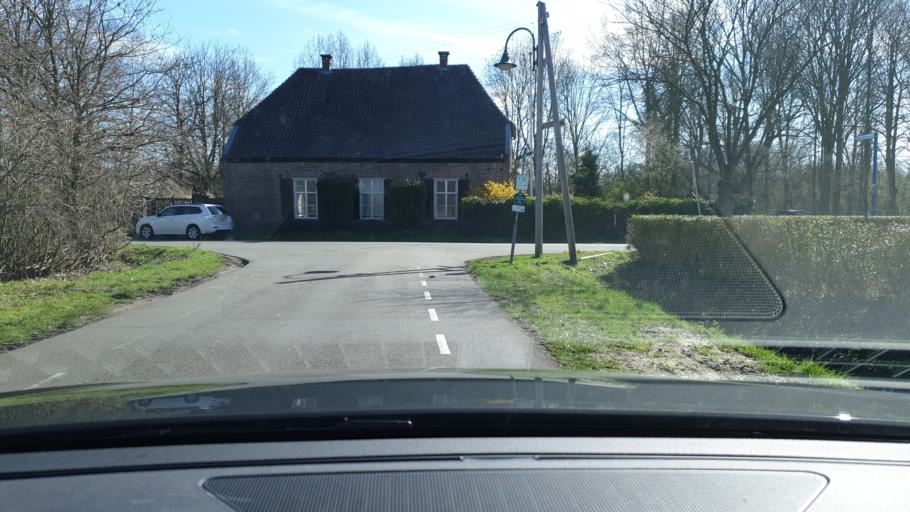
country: NL
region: North Brabant
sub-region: Gemeente Eindhoven
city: Muschberg en Geestenberg
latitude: 51.4459
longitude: 5.5366
